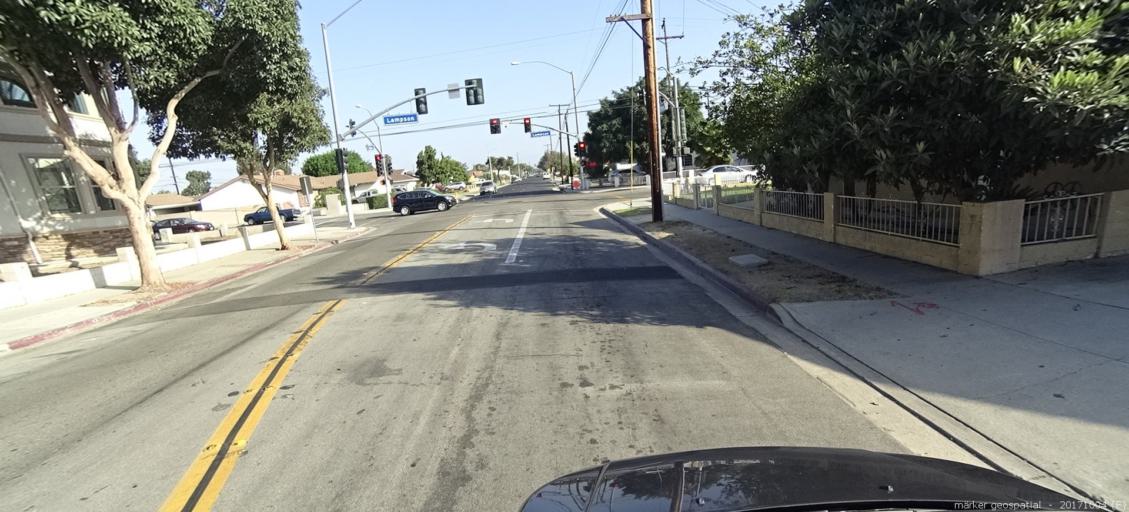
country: US
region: California
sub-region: Orange County
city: Garden Grove
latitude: 33.7813
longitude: -117.9192
